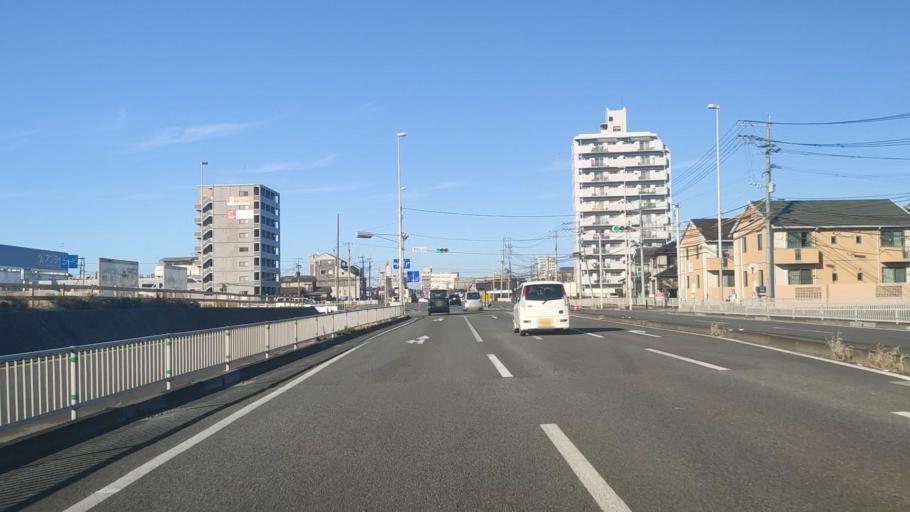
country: JP
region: Oita
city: Oita
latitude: 33.2296
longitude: 131.6189
